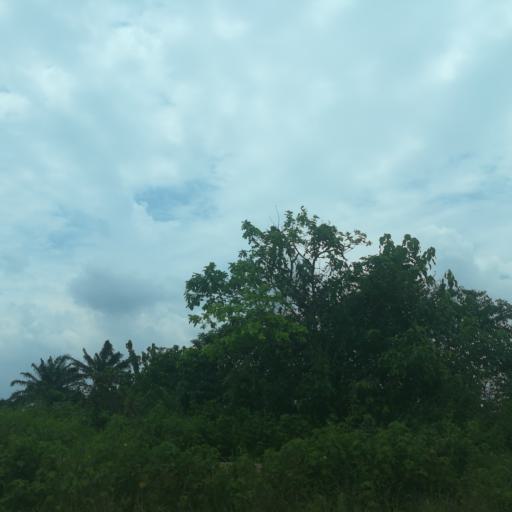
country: NG
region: Lagos
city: Ejirin
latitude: 6.6670
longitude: 3.7935
